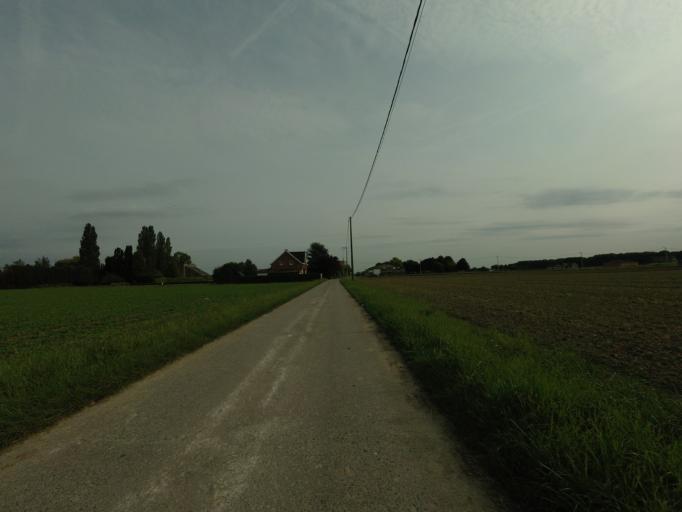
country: BE
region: Flanders
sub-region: Provincie Vlaams-Brabant
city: Kampenhout
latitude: 50.9446
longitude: 4.5377
